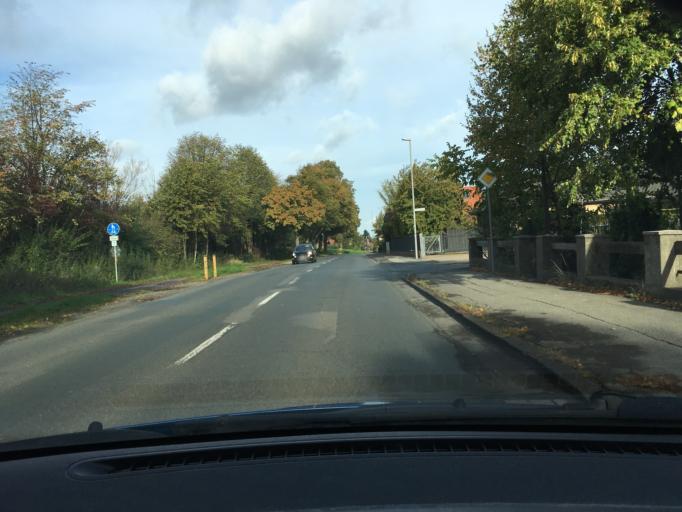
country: DE
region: Lower Saxony
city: Barsinghausen
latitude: 52.3160
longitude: 9.4364
